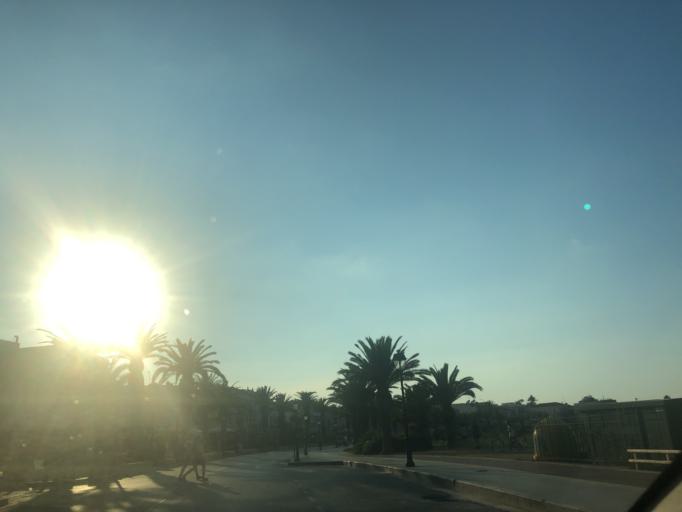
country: GR
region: Crete
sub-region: Nomos Rethymnis
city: Rethymno
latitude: 35.3676
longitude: 24.4785
